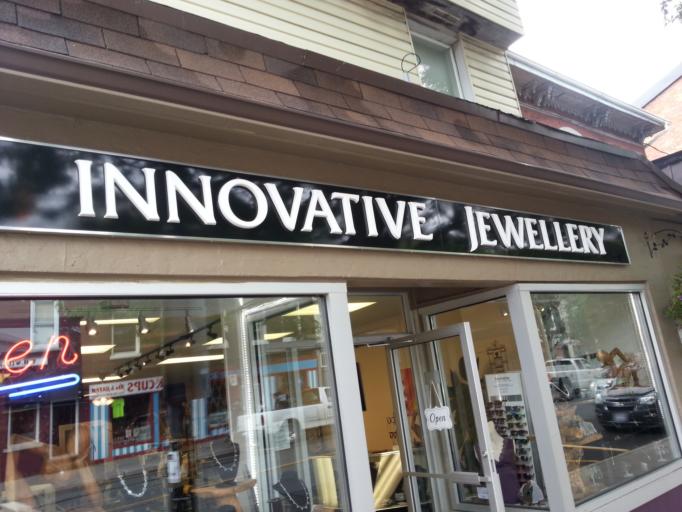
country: CA
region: Ontario
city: Picton
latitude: 44.0071
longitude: -77.1426
